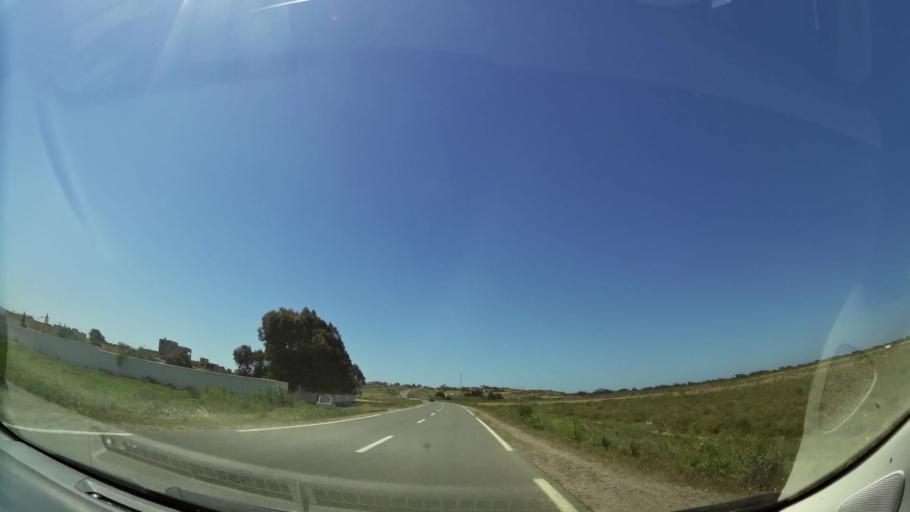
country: MA
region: Oriental
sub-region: Berkane-Taourirt
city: Madagh
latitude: 35.1188
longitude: -2.3731
